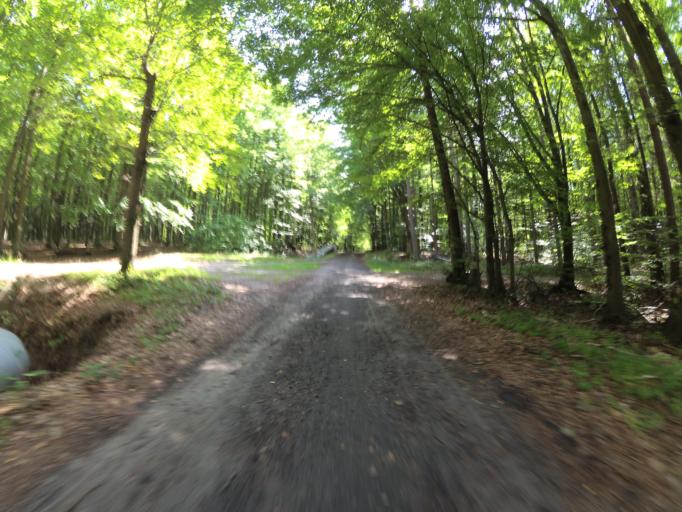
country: PL
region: Pomeranian Voivodeship
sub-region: Gdynia
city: Wielki Kack
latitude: 54.5049
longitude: 18.4923
